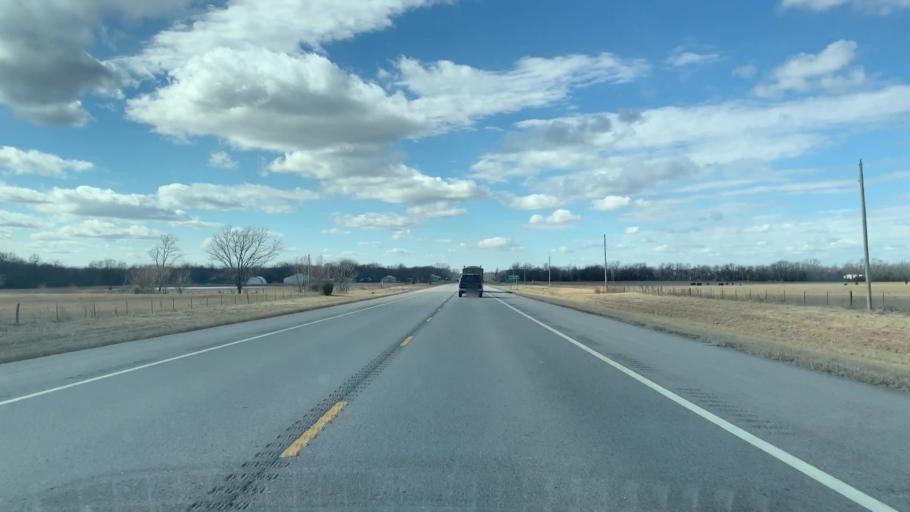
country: US
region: Kansas
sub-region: Cherokee County
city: Columbus
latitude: 37.3401
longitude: -94.9159
